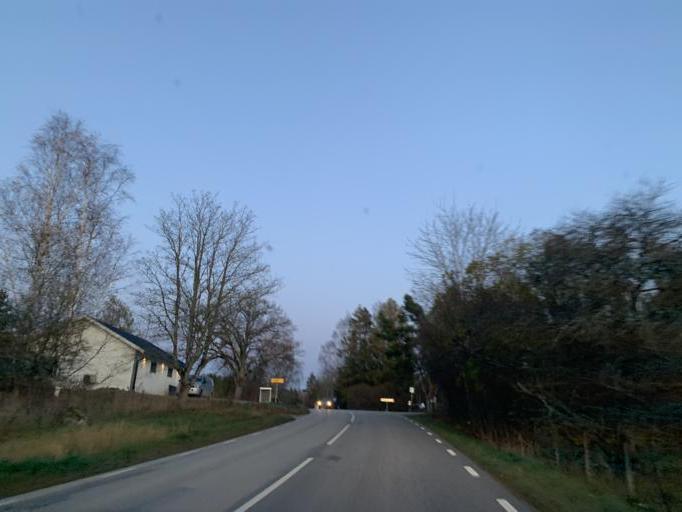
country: SE
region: OErebro
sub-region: Lindesbergs Kommun
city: Frovi
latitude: 59.3256
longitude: 15.4557
